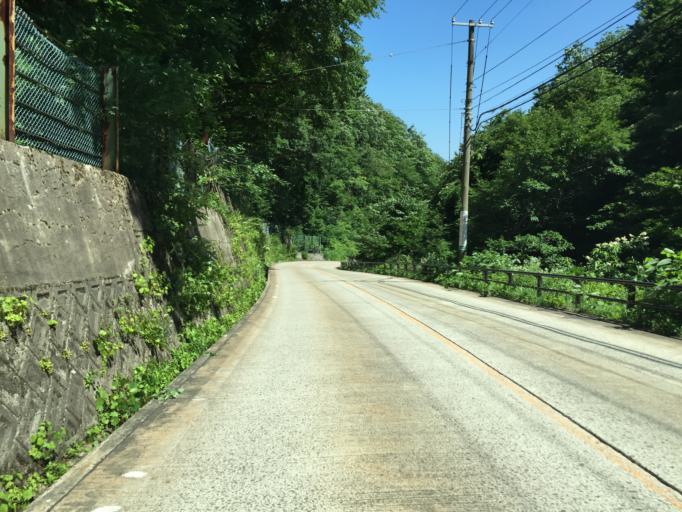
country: JP
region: Fukushima
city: Fukushima-shi
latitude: 37.7520
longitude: 140.3139
